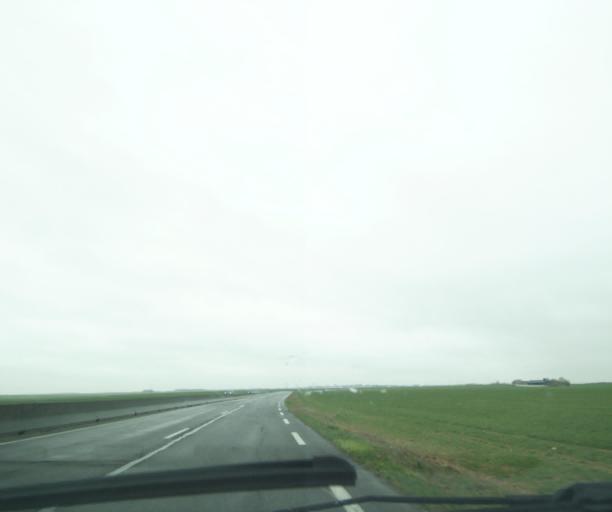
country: FR
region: Ile-de-France
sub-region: Departement de l'Essonne
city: Angerville
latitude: 48.3360
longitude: 2.0343
